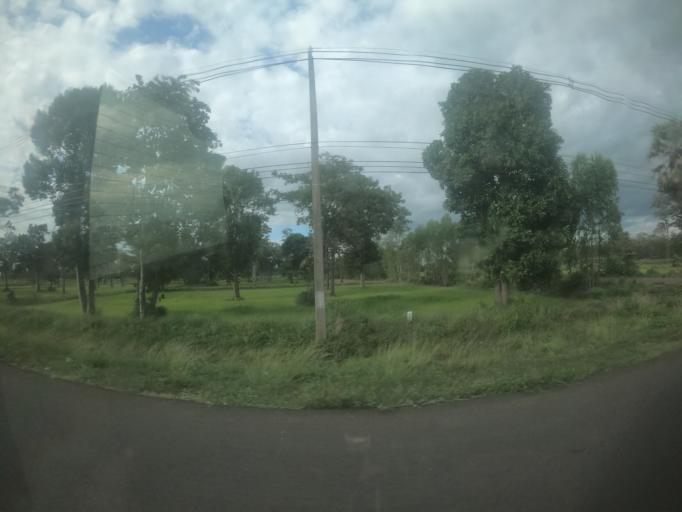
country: TH
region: Surin
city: Prasat
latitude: 14.5729
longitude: 103.4856
